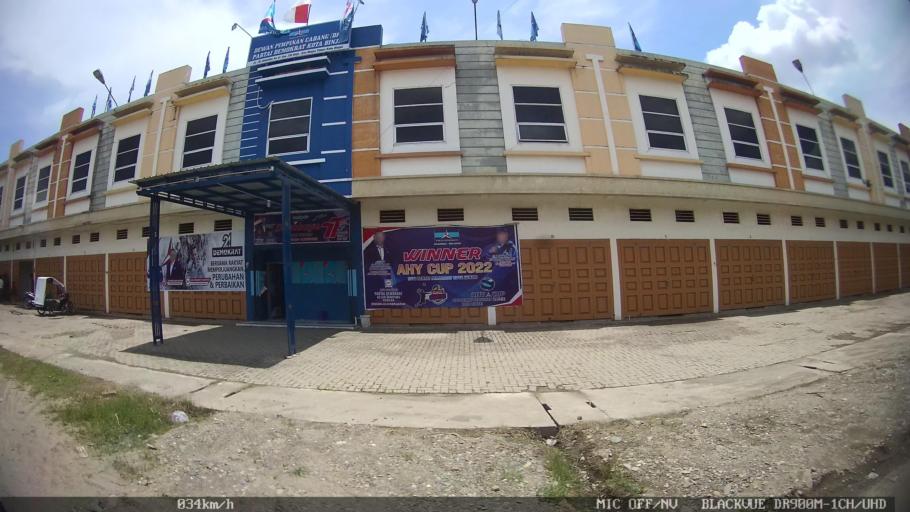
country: ID
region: North Sumatra
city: Binjai
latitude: 3.6231
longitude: 98.5185
